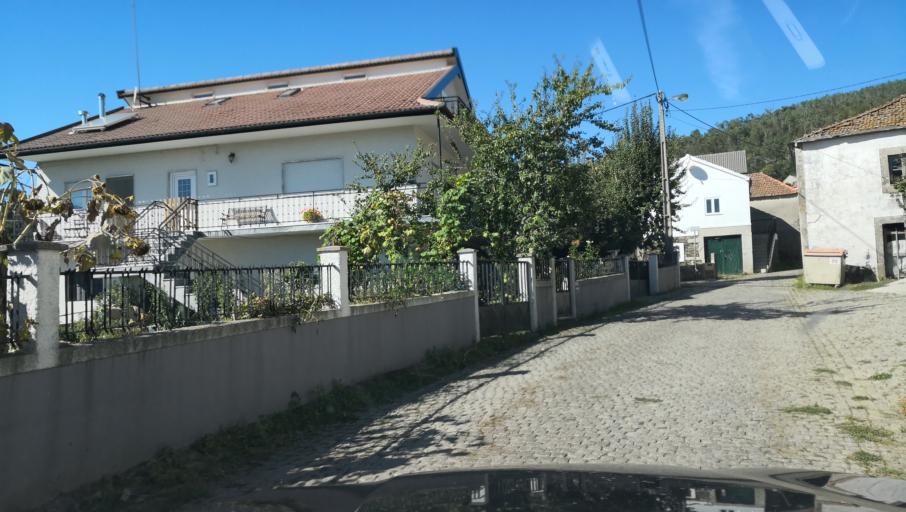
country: PT
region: Vila Real
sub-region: Santa Marta de Penaguiao
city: Santa Marta de Penaguiao
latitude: 41.2916
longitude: -7.8572
